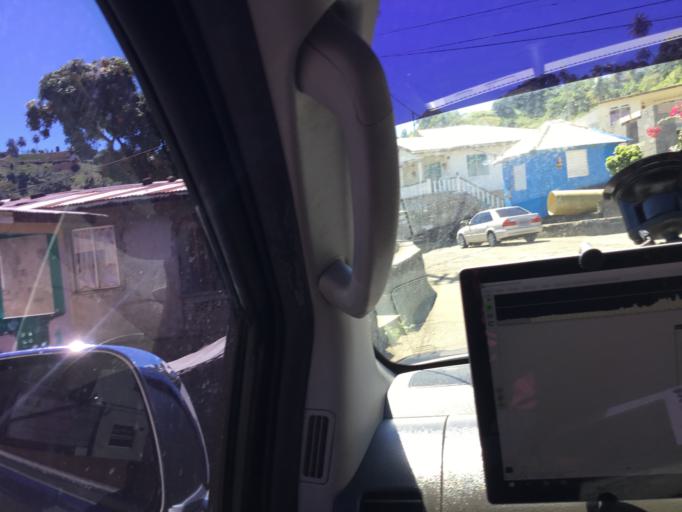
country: VC
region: Charlotte
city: Byera Village
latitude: 13.2471
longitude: -61.1413
